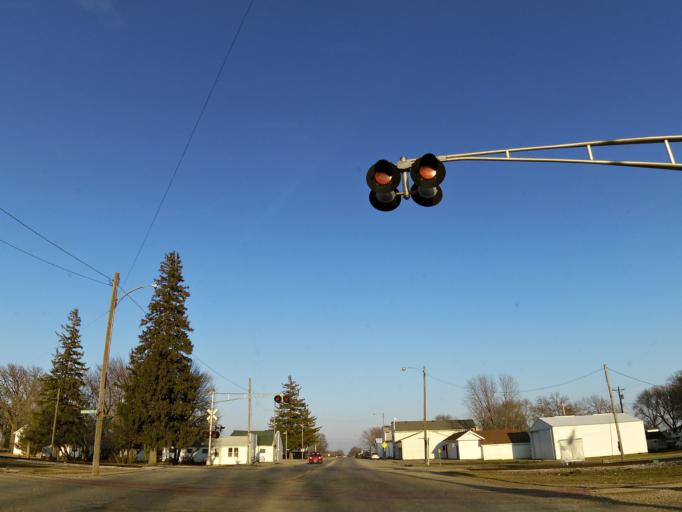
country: US
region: Iowa
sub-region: Mitchell County
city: Saint Ansgar
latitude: 43.4150
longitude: -93.0177
